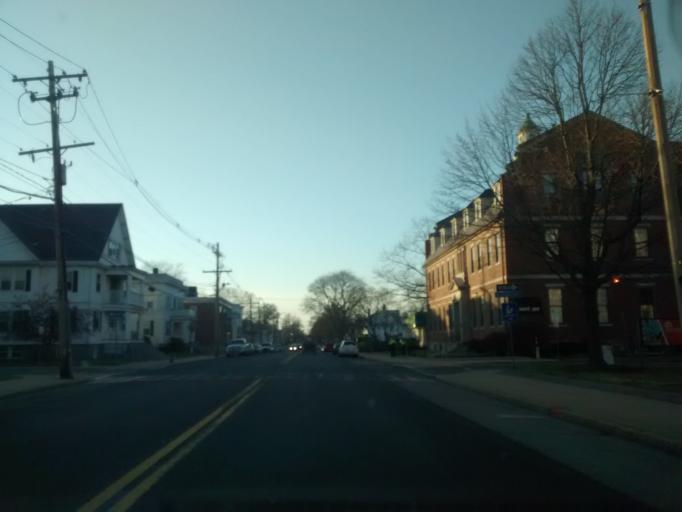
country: US
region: Massachusetts
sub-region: Middlesex County
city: Framingham
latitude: 42.2813
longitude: -71.4186
